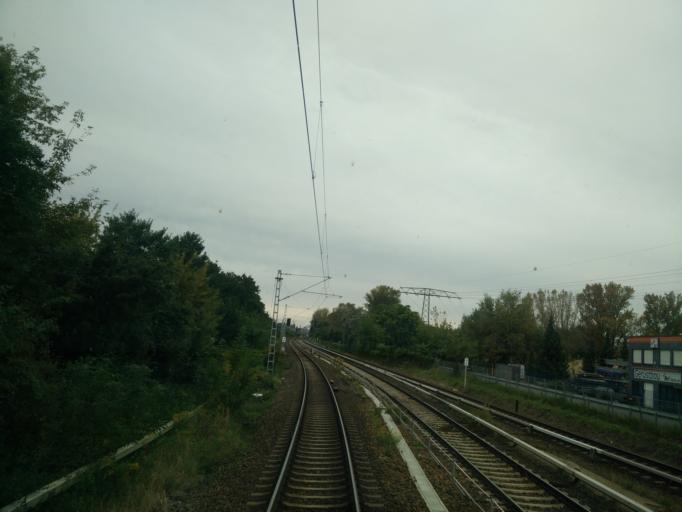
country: DE
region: Berlin
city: Rummelsburg
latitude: 52.4945
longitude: 13.4964
